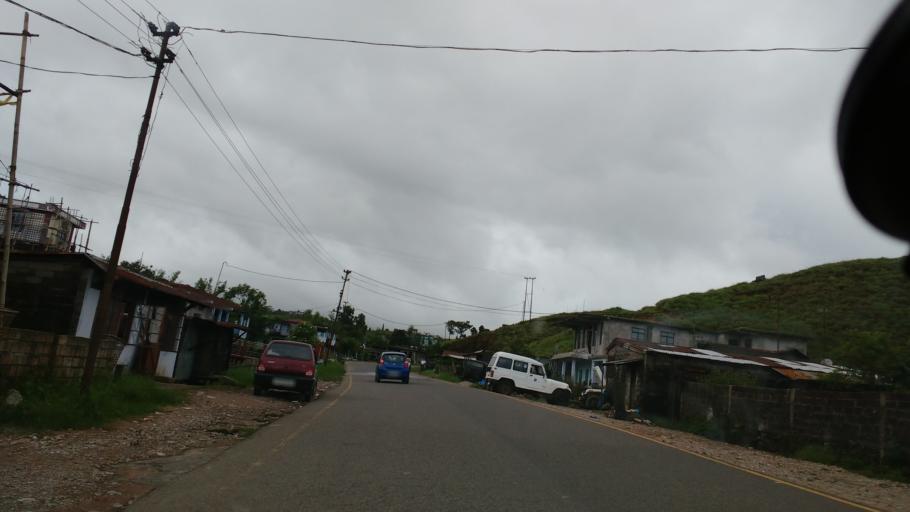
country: IN
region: Meghalaya
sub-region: East Khasi Hills
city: Cherrapunji
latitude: 25.2731
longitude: 91.7327
